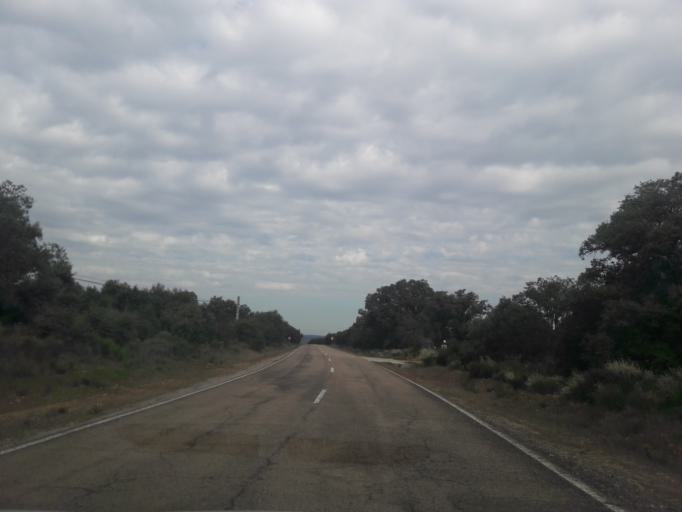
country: ES
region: Castille and Leon
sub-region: Provincia de Salamanca
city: Ciudad Rodrigo
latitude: 40.5737
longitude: -6.5311
